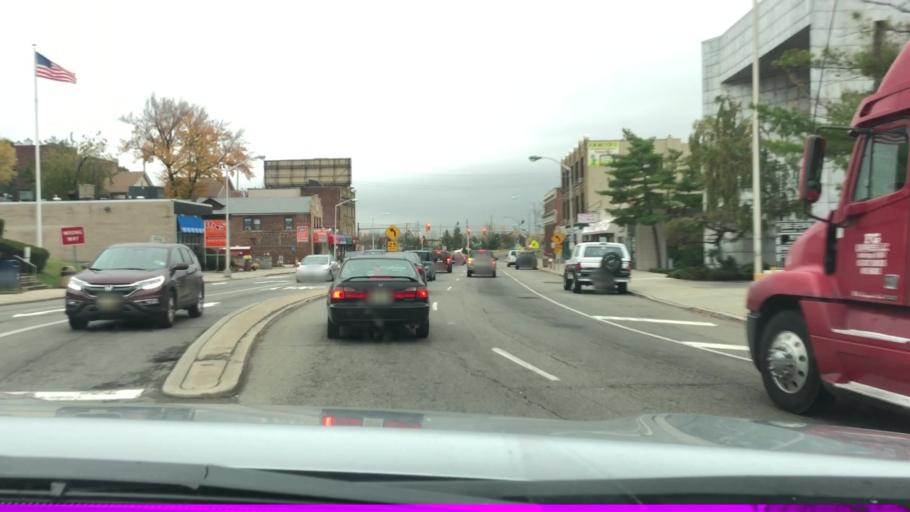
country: US
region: New Jersey
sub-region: Bergen County
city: Ridgefield
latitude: 40.8346
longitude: -74.0091
